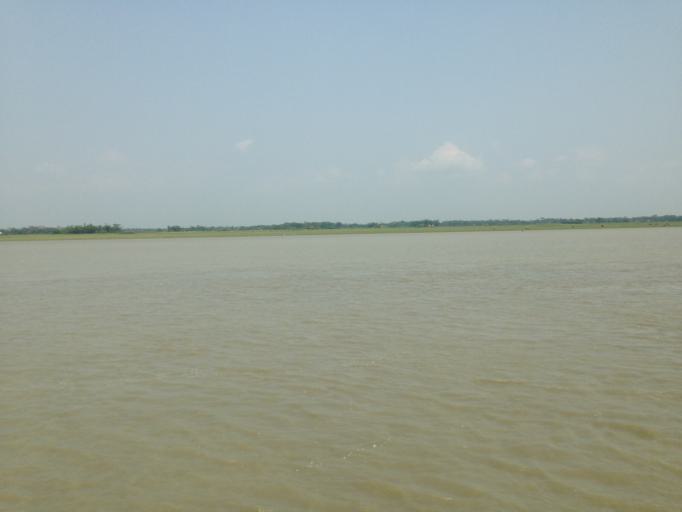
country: BD
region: Chittagong
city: Lakshmipur
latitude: 22.8568
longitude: 90.7574
